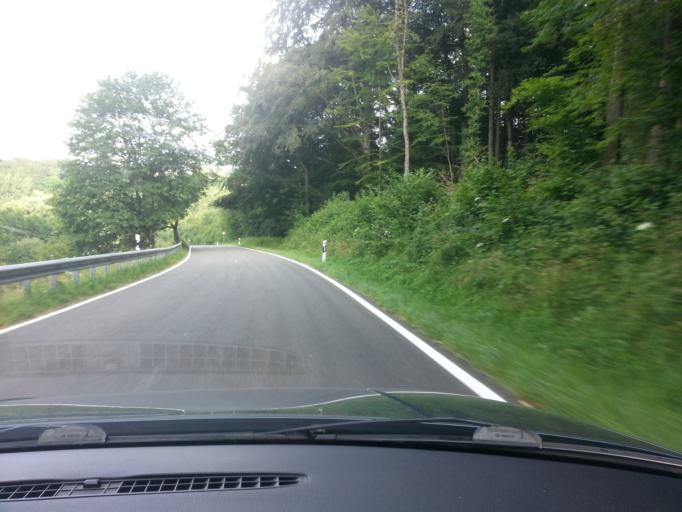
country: DE
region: Rheinland-Pfalz
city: Riedelberg
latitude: 49.1883
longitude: 7.4400
